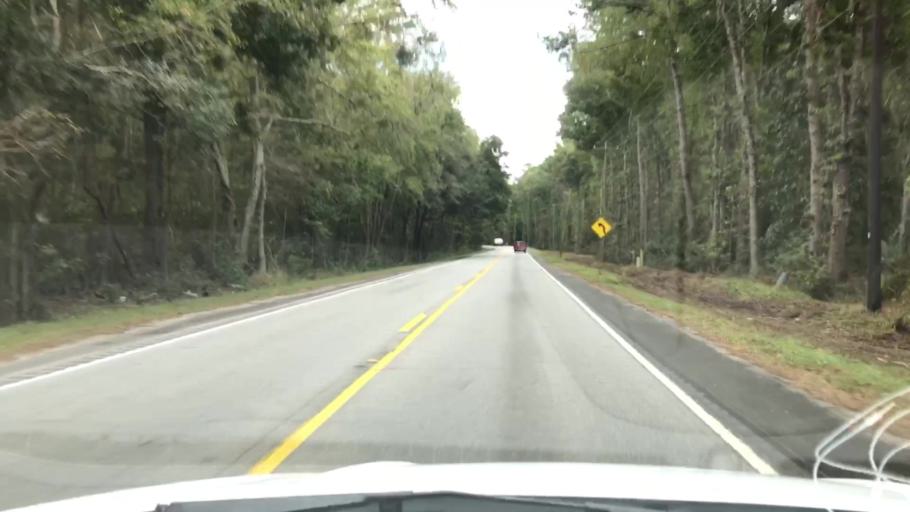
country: US
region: South Carolina
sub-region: Beaufort County
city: Bluffton
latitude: 32.2304
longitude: -80.9143
